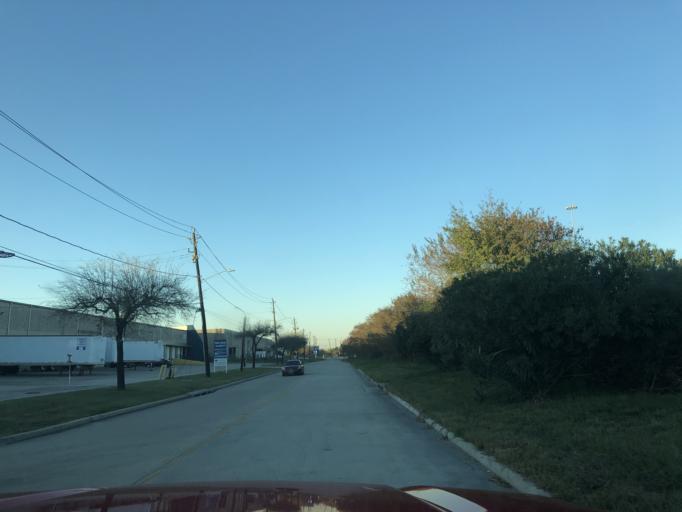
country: US
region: Texas
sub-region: Harris County
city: Jacinto City
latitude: 29.7556
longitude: -95.2656
